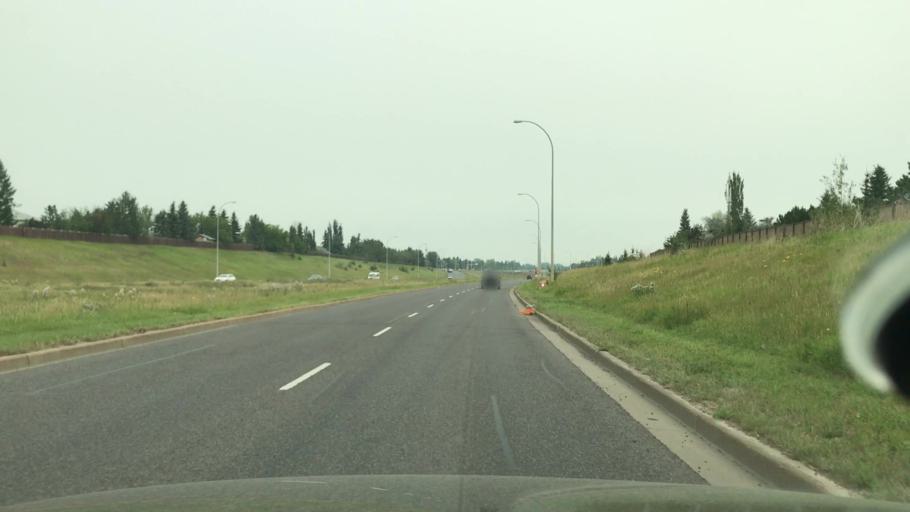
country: CA
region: Alberta
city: Edmonton
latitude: 53.4709
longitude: -113.5791
